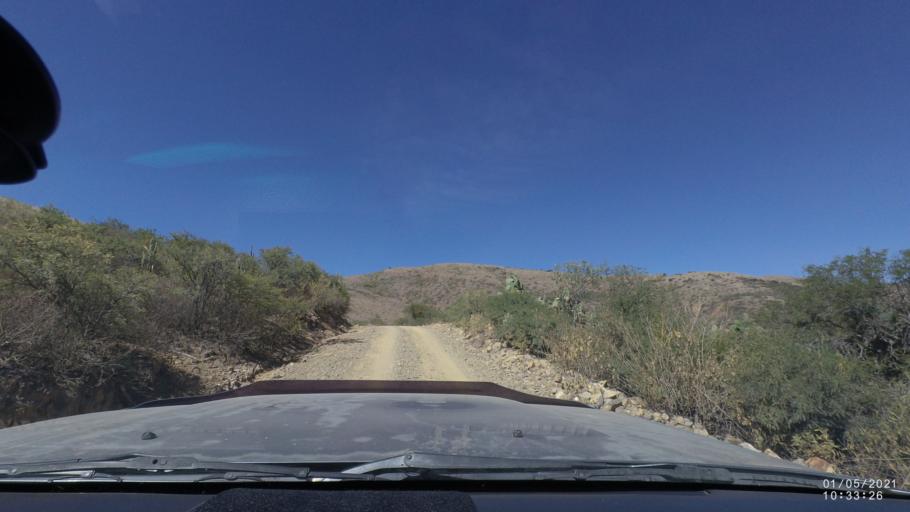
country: BO
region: Cochabamba
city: Capinota
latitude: -17.5969
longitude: -66.1940
